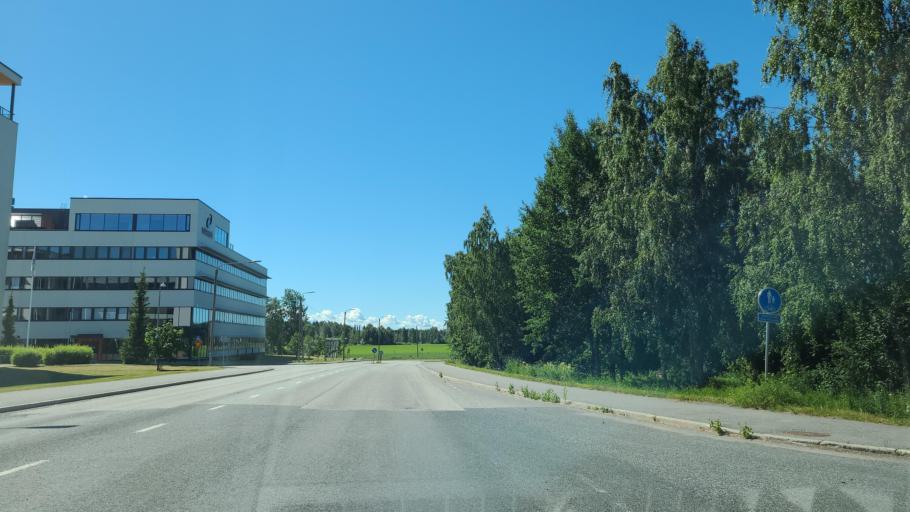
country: FI
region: Ostrobothnia
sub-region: Vaasa
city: Ristinummi
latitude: 63.0576
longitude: 21.7316
